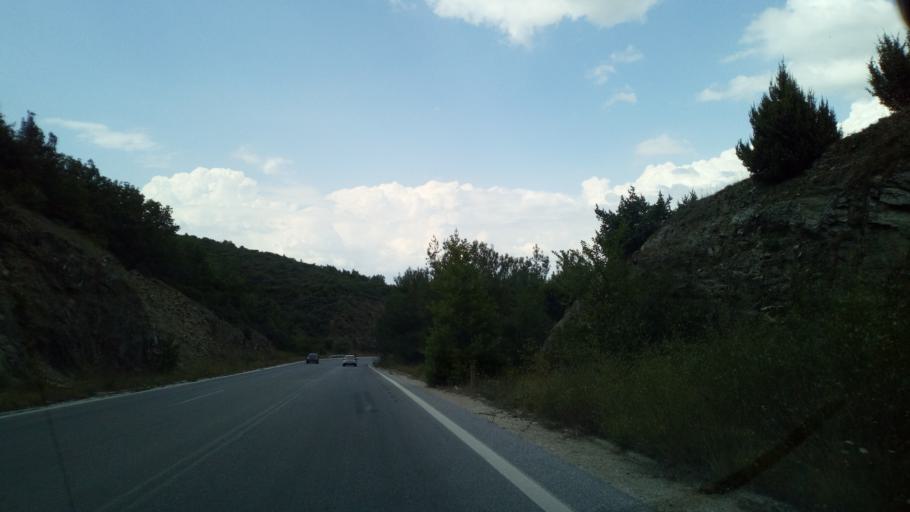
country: GR
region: Central Macedonia
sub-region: Nomos Chalkidikis
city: Polygyros
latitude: 40.4186
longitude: 23.4212
